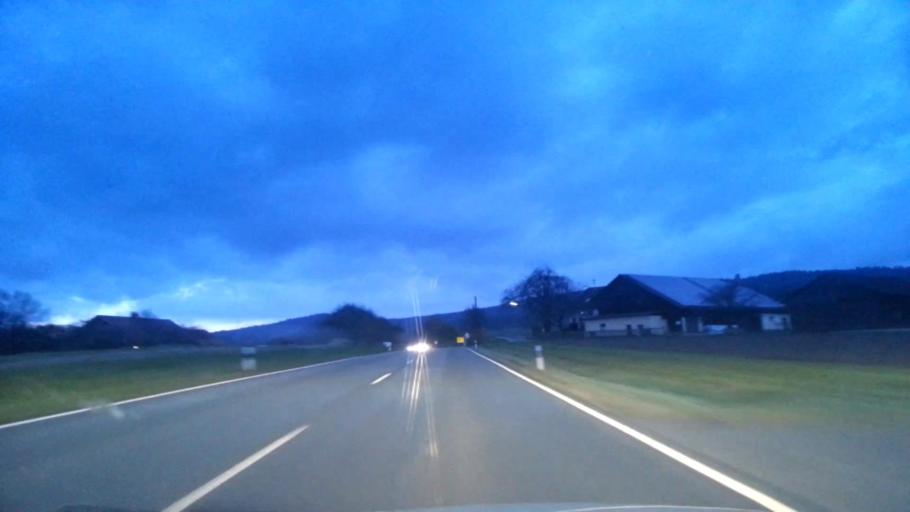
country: DE
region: Bavaria
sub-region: Upper Franconia
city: Kirchenpingarten
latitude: 49.9176
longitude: 11.8224
